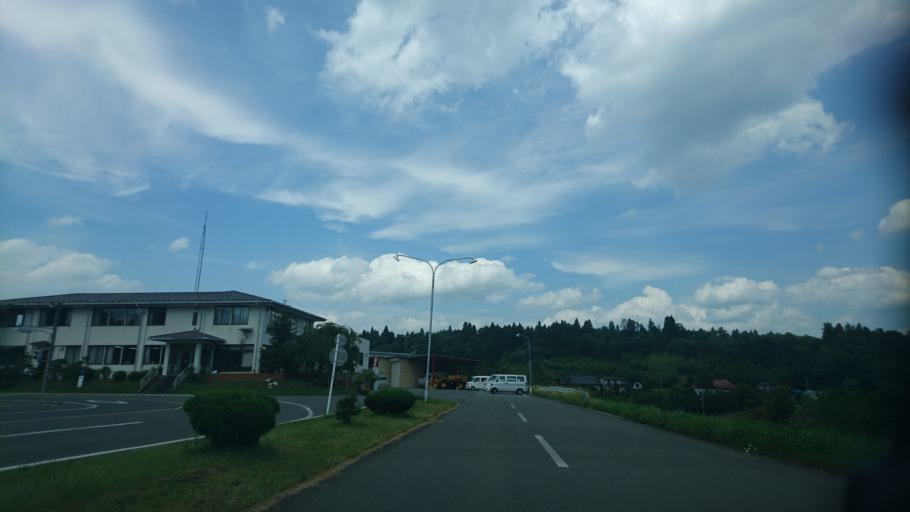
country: JP
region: Iwate
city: Ichinoseki
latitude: 38.9064
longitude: 141.3541
